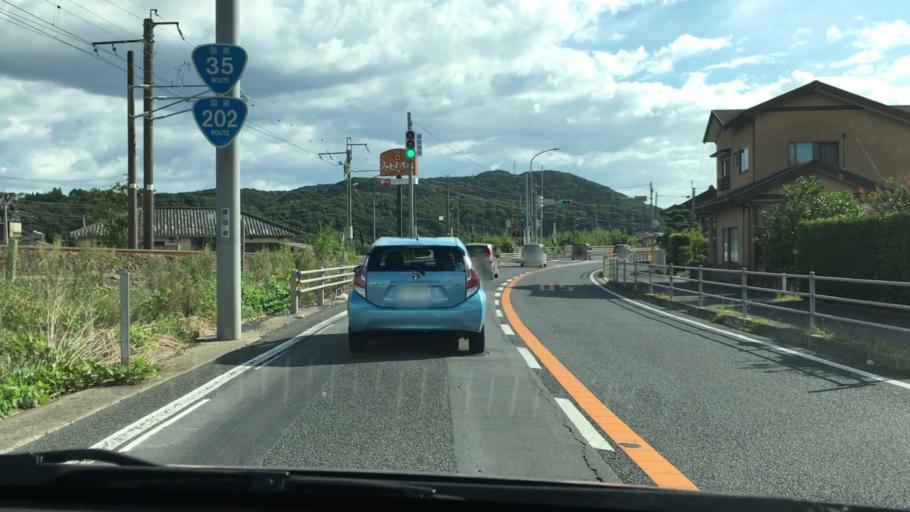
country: JP
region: Nagasaki
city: Sasebo
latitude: 33.1465
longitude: 129.8276
